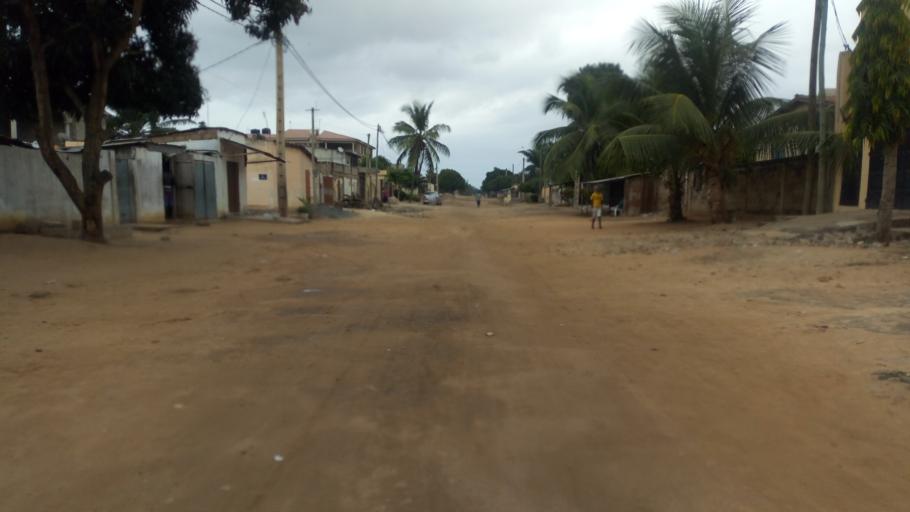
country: TG
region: Maritime
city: Lome
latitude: 6.1775
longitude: 1.1814
